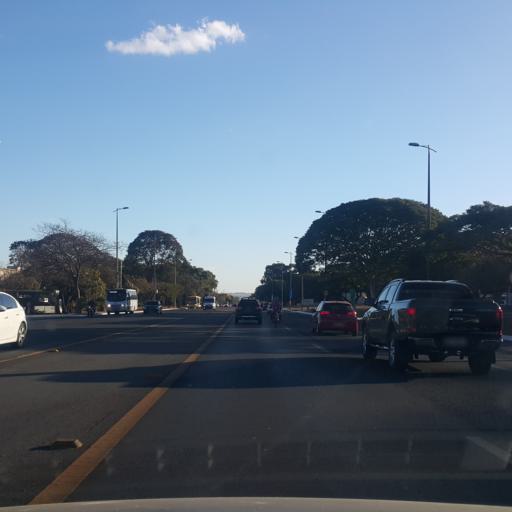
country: BR
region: Federal District
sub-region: Brasilia
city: Brasilia
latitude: -15.8256
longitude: -47.9127
